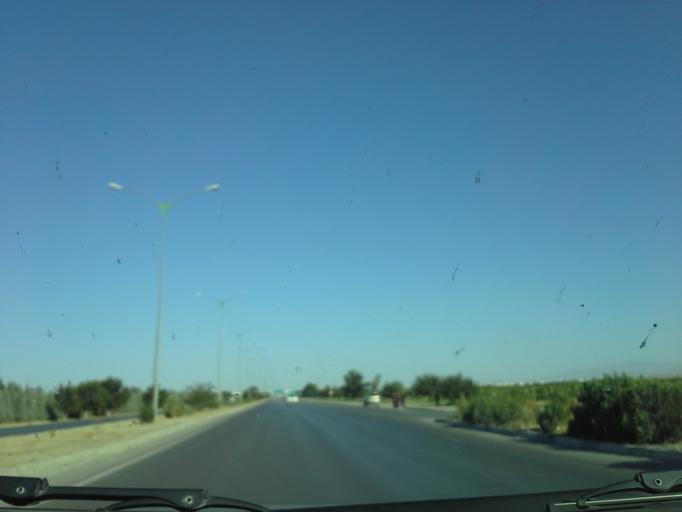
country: TM
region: Ahal
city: Abadan
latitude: 38.0938
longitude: 58.0976
